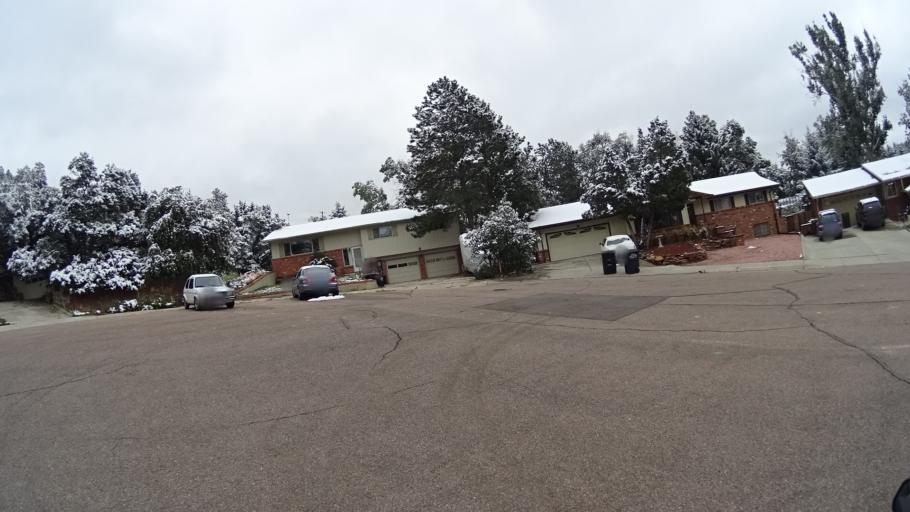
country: US
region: Colorado
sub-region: El Paso County
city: Colorado Springs
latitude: 38.8927
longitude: -104.7802
